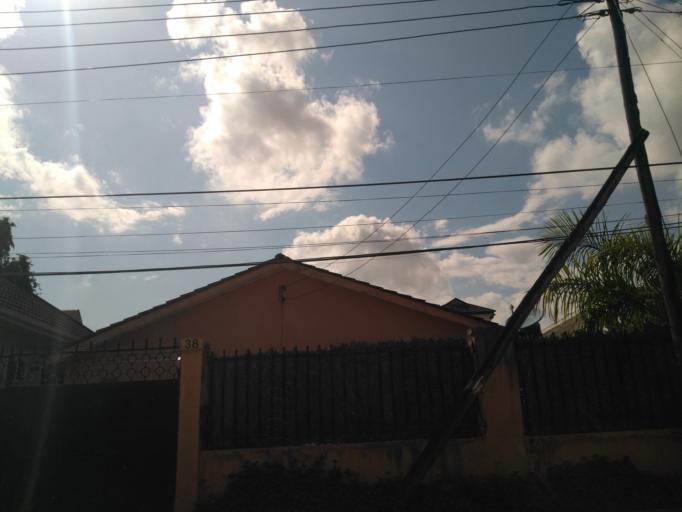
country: TZ
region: Dar es Salaam
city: Magomeni
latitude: -6.7634
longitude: 39.2489
